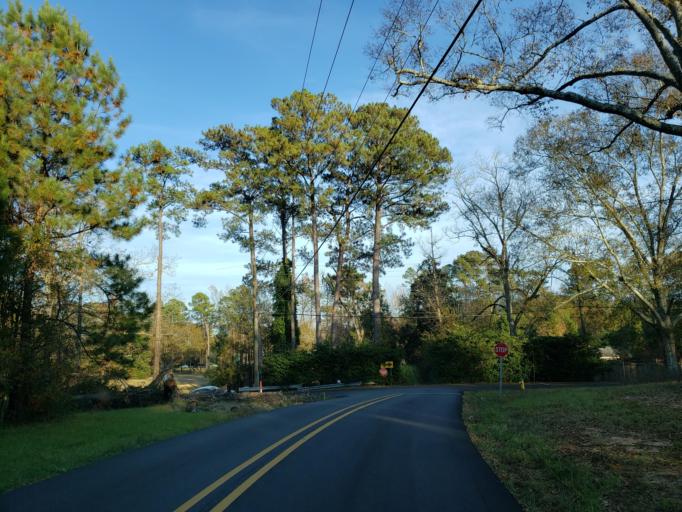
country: US
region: Mississippi
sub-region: Lamar County
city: Arnold Line
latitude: 31.3493
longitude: -89.3538
